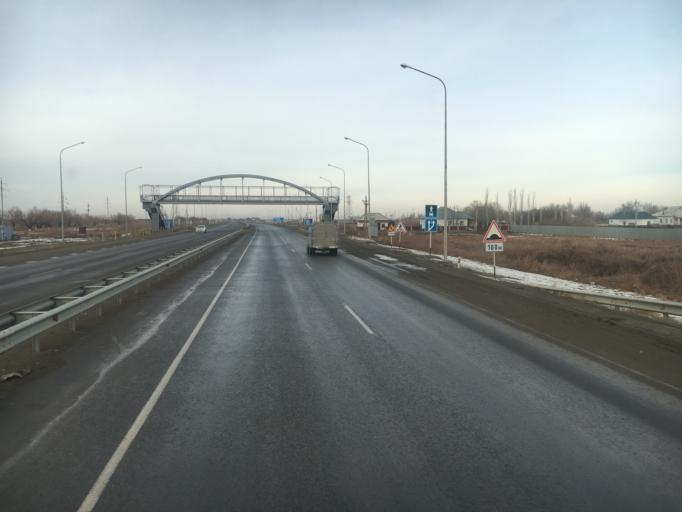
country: KZ
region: Qyzylorda
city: Shieli
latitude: 44.1373
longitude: 66.9692
